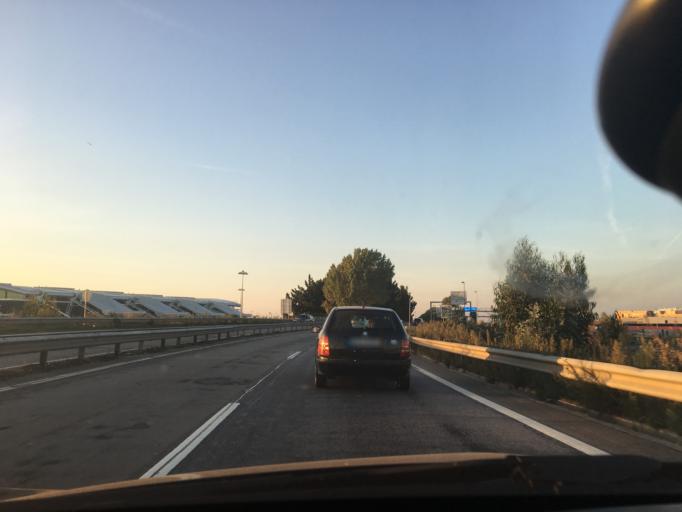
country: PT
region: Porto
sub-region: Matosinhos
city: Santa Cruz do Bispo
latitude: 41.2347
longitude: -8.6672
